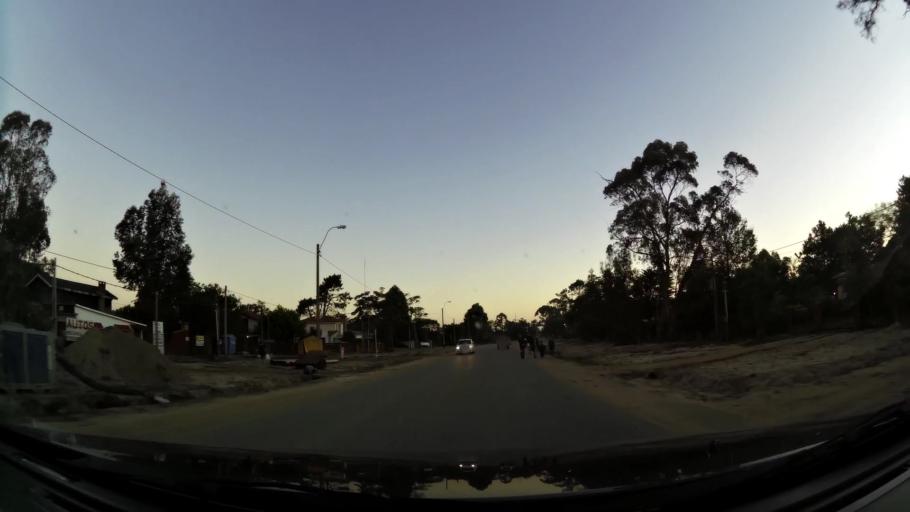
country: UY
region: Canelones
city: Colonia Nicolich
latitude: -34.8243
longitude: -55.9568
